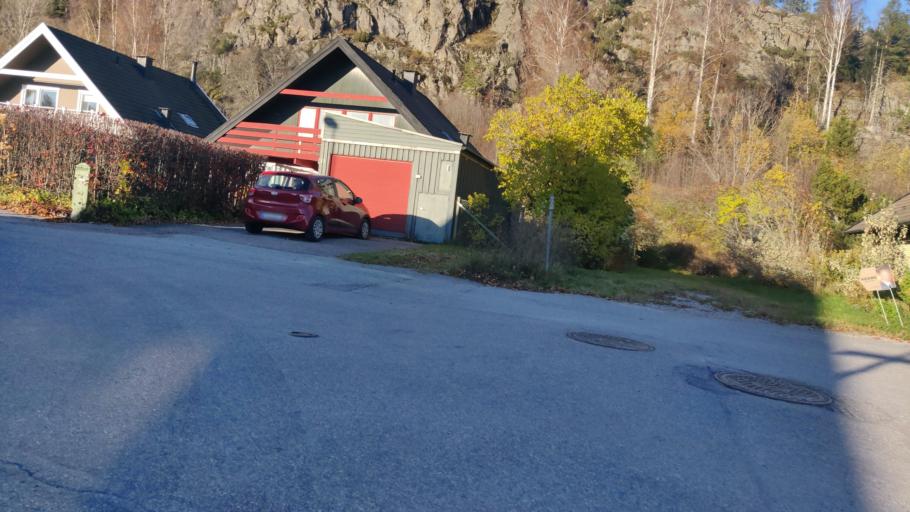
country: SE
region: Vaesternorrland
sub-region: Sundsvalls Kommun
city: Nolby
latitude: 62.2755
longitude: 17.3624
